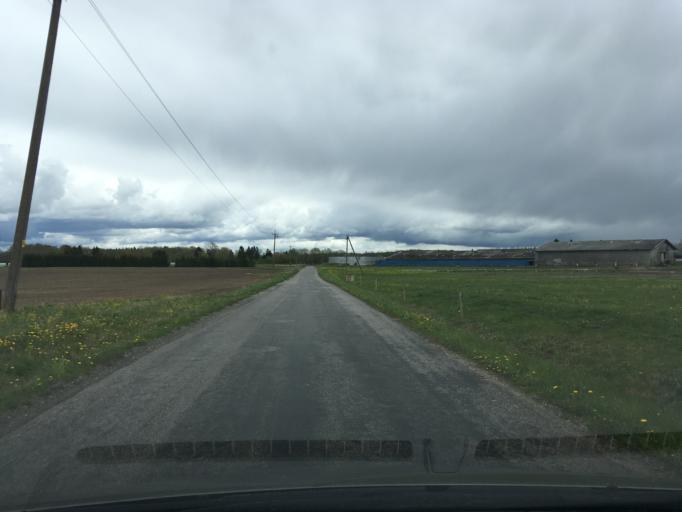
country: EE
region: Harju
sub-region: Joelaehtme vald
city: Loo
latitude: 59.3671
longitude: 24.9643
